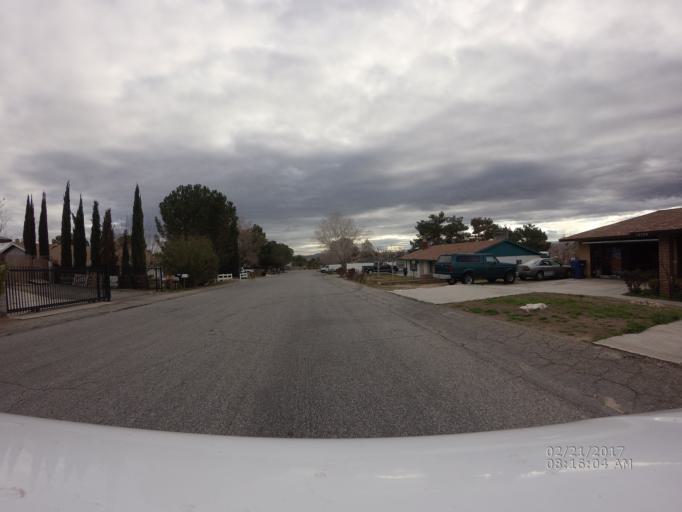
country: US
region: California
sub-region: Los Angeles County
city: Lake Los Angeles
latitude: 34.5981
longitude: -117.8361
